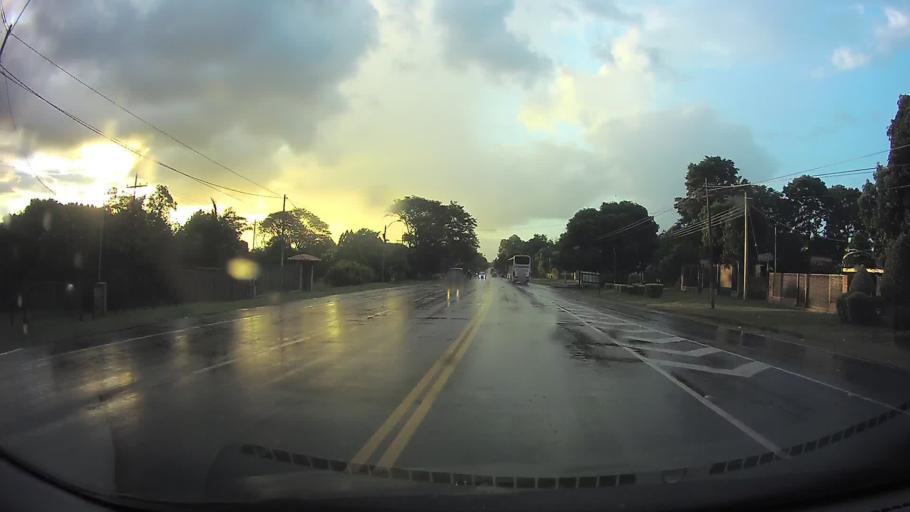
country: PY
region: Paraguari
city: Paraguari
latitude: -25.6033
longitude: -57.1883
